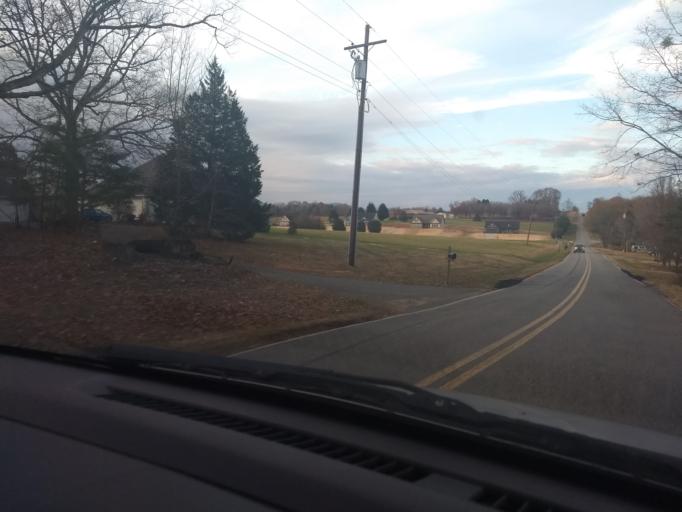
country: US
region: South Carolina
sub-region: Greenville County
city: Greer
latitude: 35.0244
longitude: -82.2016
